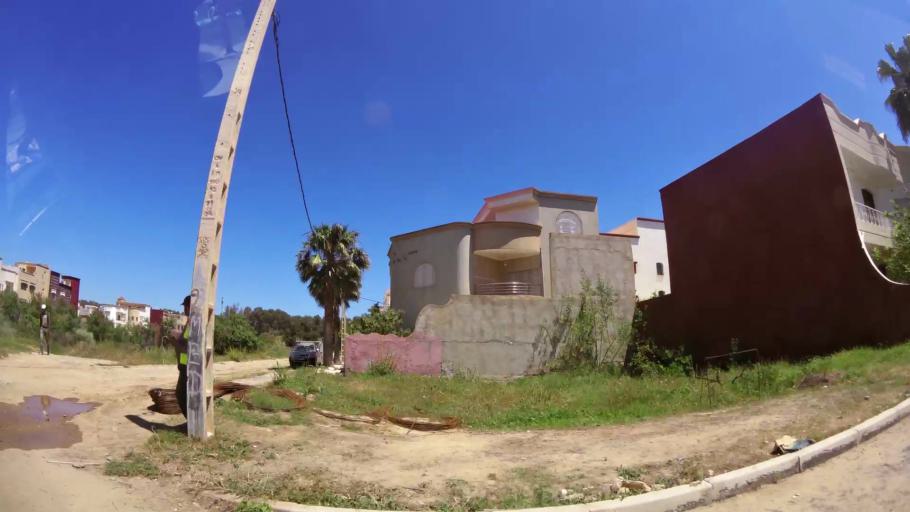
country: MA
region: Oriental
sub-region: Berkane-Taourirt
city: Madagh
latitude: 35.0864
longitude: -2.2446
